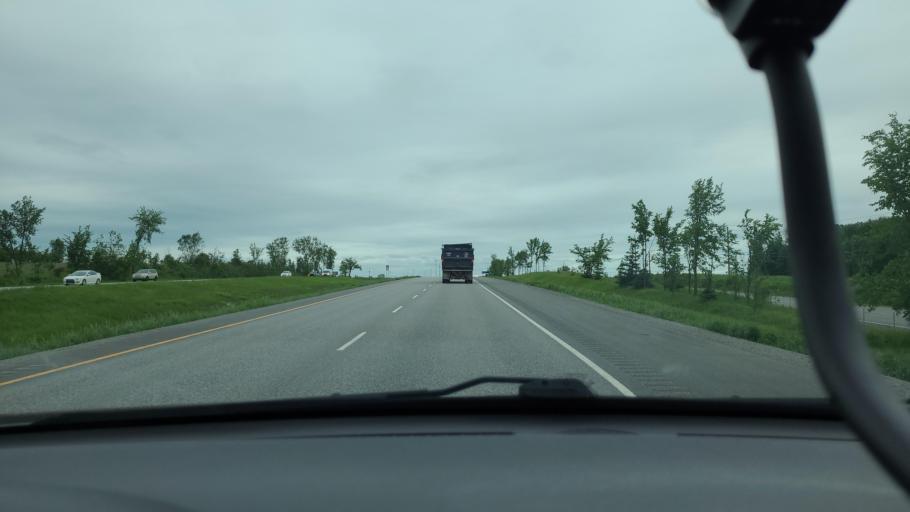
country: CA
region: Quebec
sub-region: Lanaudiere
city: Mascouche
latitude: 45.8351
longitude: -73.6181
